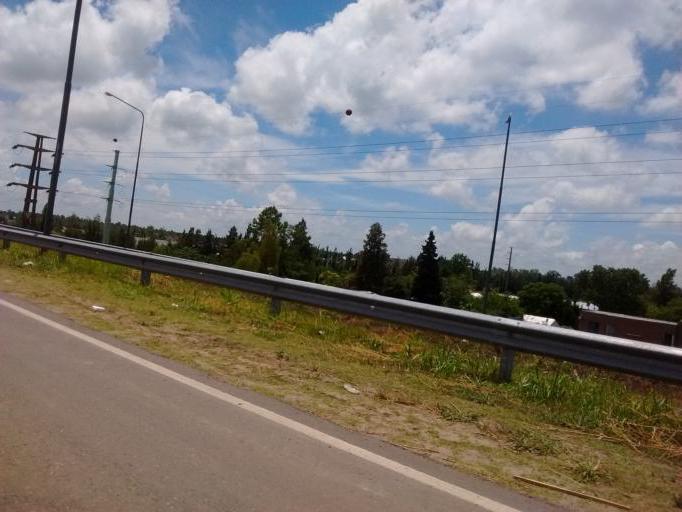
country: AR
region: Santa Fe
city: Funes
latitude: -32.9238
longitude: -60.7773
